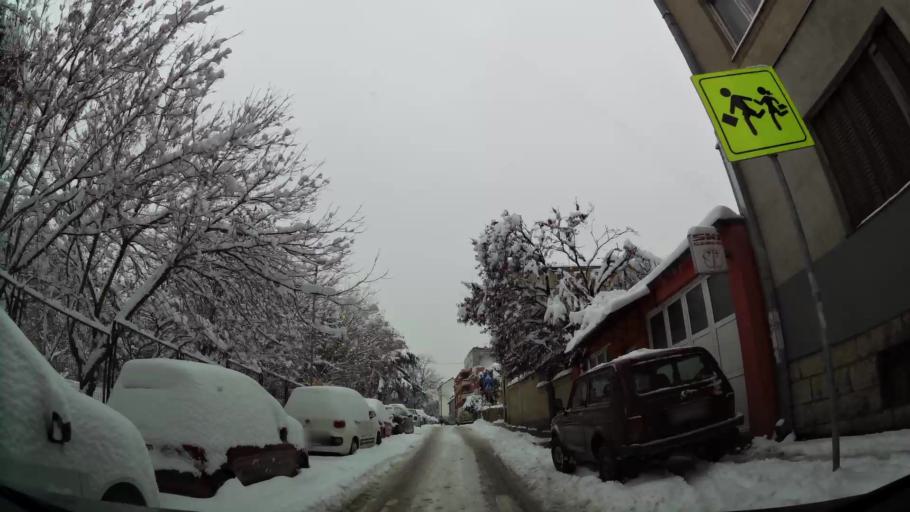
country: RS
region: Central Serbia
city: Belgrade
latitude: 44.8123
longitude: 20.4831
